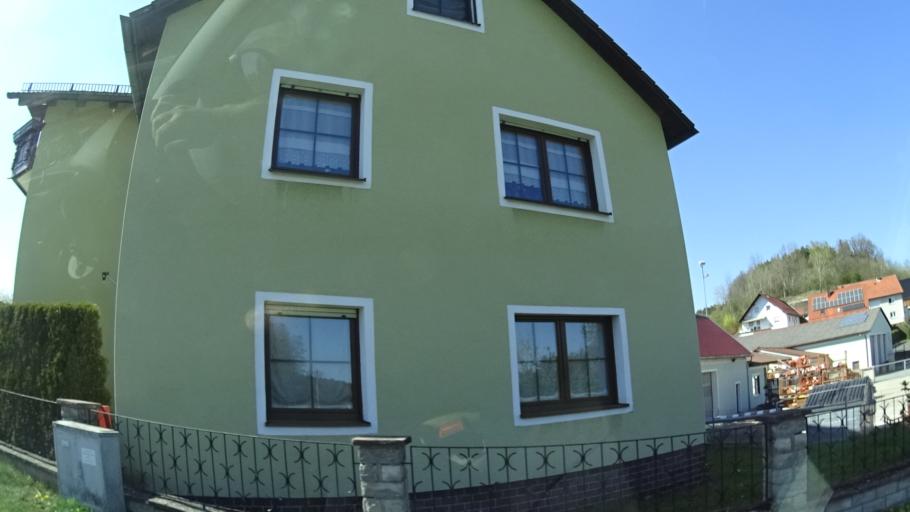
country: DE
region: Bavaria
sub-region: Upper Palatinate
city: Edelsfeld
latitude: 49.5468
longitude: 11.7289
